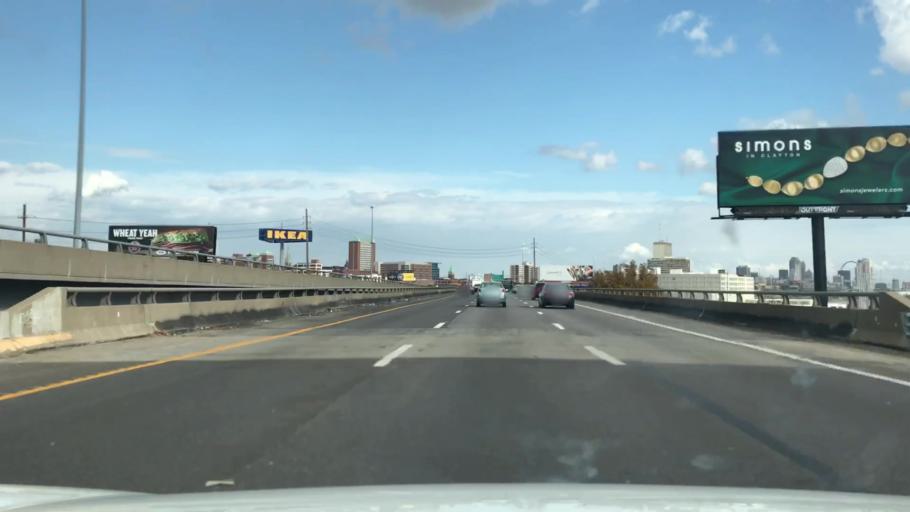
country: US
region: Missouri
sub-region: City of Saint Louis
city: St. Louis
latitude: 38.6315
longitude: -90.2472
